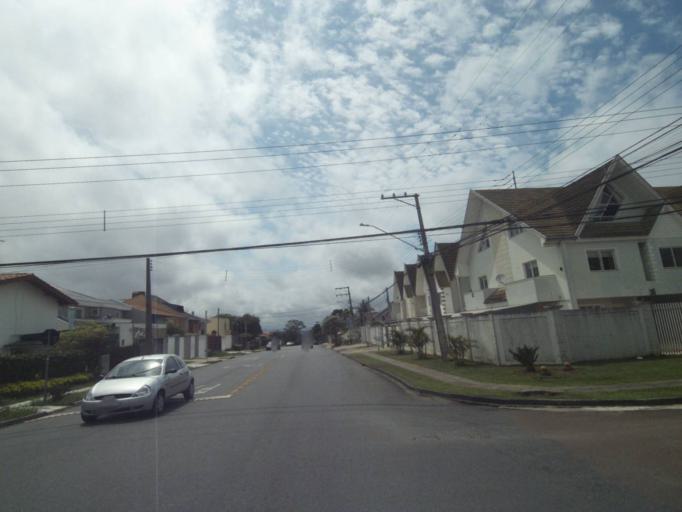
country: BR
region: Parana
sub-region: Pinhais
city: Pinhais
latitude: -25.4328
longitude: -49.2279
